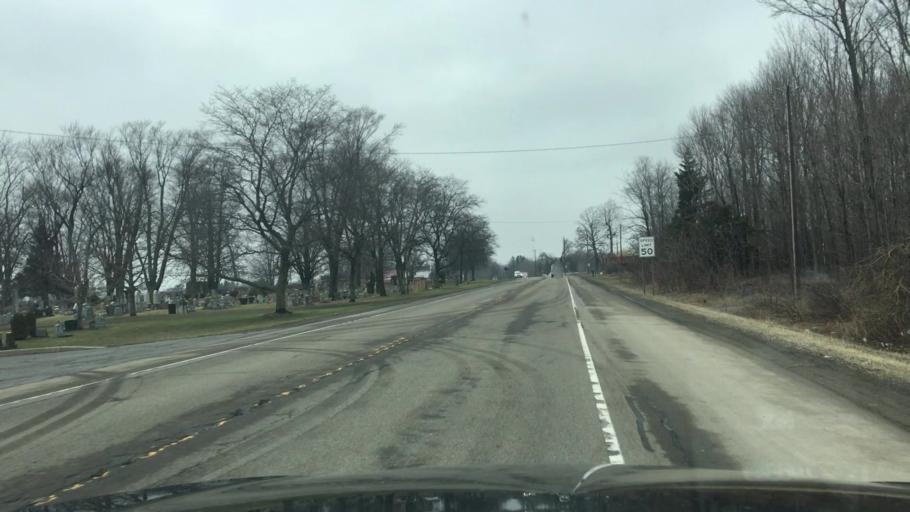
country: US
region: New York
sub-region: Chautauqua County
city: Fredonia
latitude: 42.4400
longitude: -79.3055
